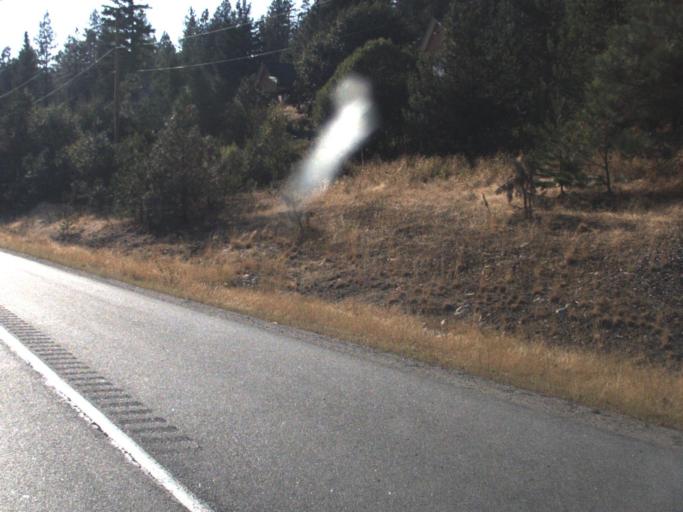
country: US
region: Washington
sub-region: Pend Oreille County
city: Newport
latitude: 48.1519
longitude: -117.1109
